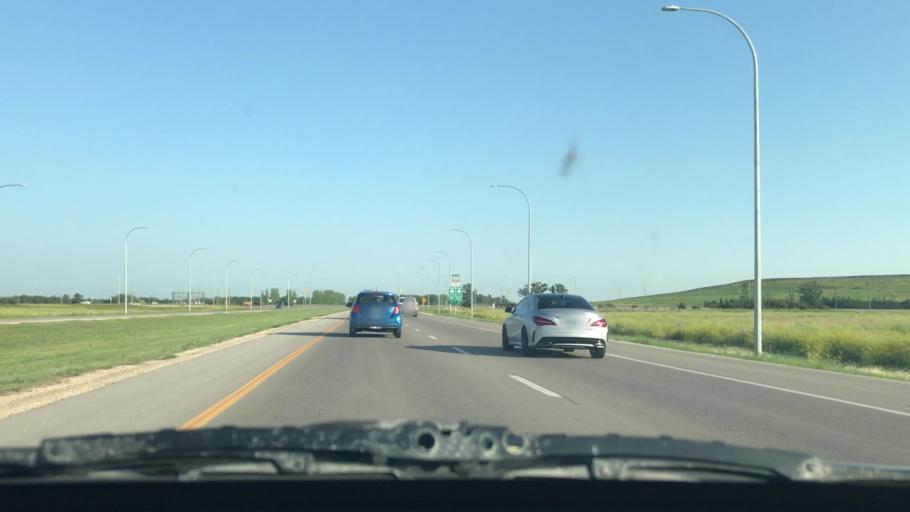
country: CA
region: Manitoba
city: Winnipeg
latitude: 49.7718
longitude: -97.1849
